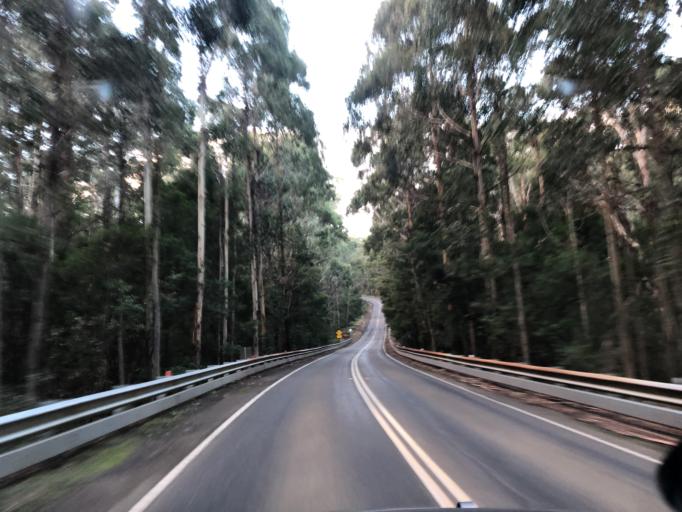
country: AU
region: Victoria
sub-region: Moorabool
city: Bacchus Marsh
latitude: -37.4353
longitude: 144.2798
